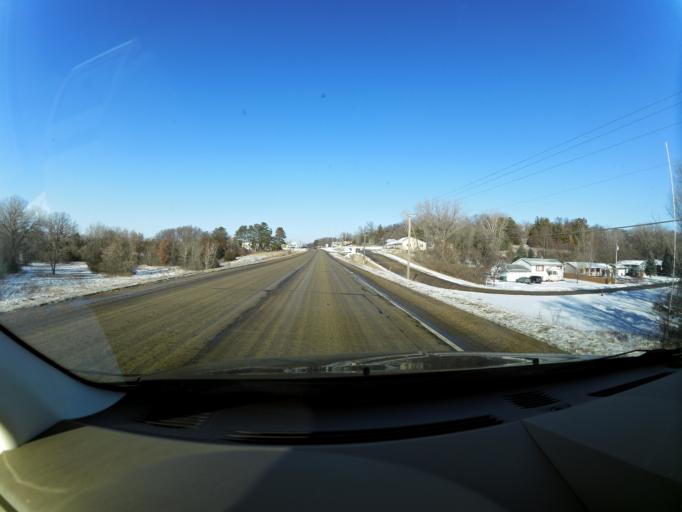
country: US
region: Minnesota
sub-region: Goodhue County
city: Cannon Falls
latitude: 44.4926
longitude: -92.9062
